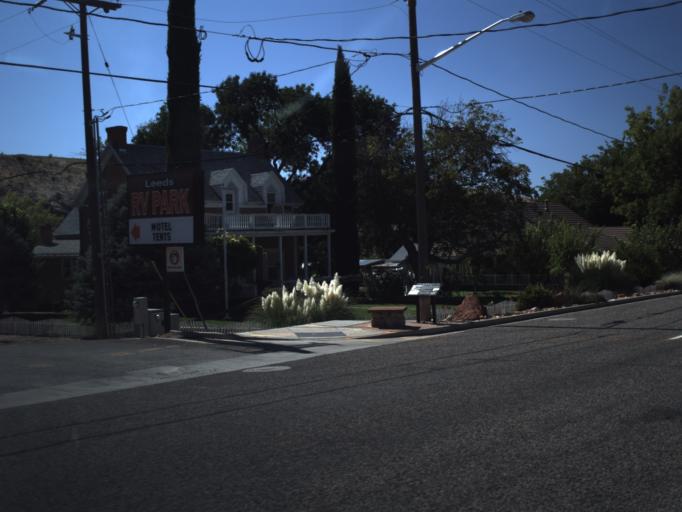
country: US
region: Utah
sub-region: Washington County
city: Toquerville
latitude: 37.2360
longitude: -113.3629
